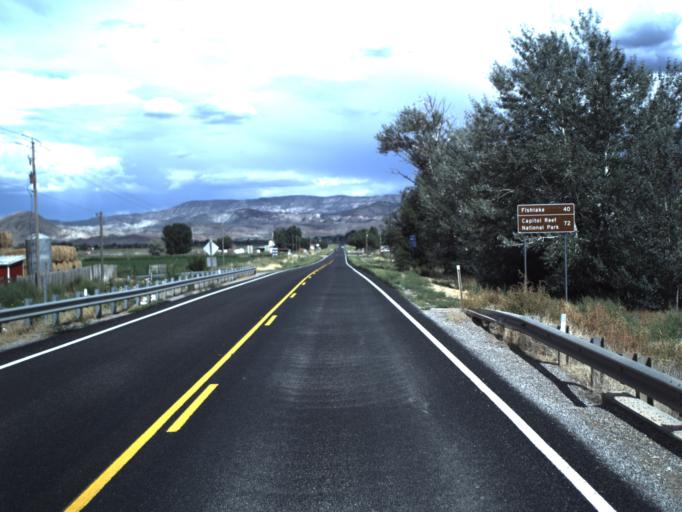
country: US
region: Utah
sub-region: Sevier County
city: Richfield
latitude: 38.7724
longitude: -112.0677
